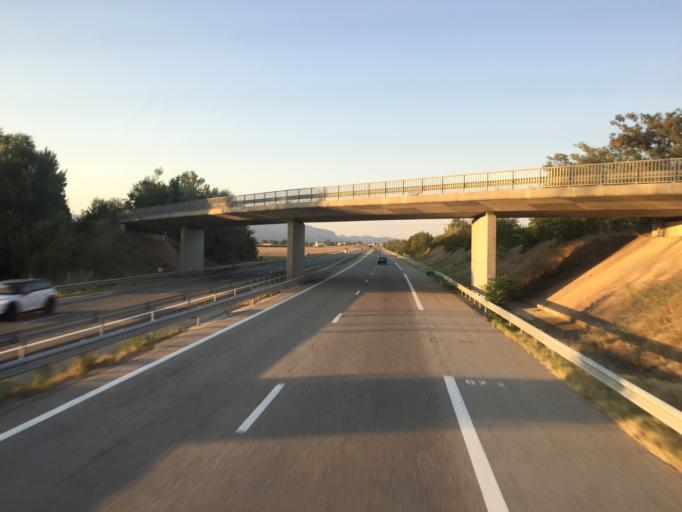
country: FR
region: Provence-Alpes-Cote d'Azur
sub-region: Departement des Alpes-de-Haute-Provence
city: Sainte-Tulle
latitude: 43.7798
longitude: 5.8028
